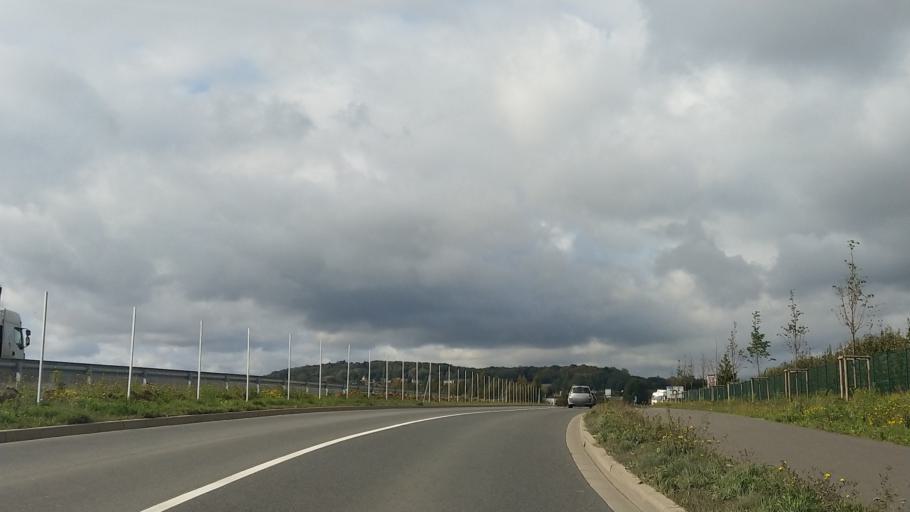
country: FR
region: Ile-de-France
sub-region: Departement du Val-d'Oise
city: Attainville
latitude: 49.0630
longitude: 2.3367
